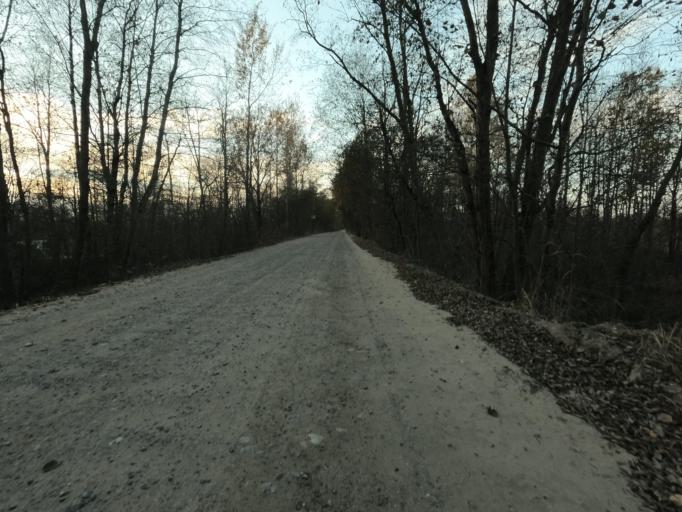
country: RU
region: Leningrad
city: Mga
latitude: 59.7688
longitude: 31.2338
